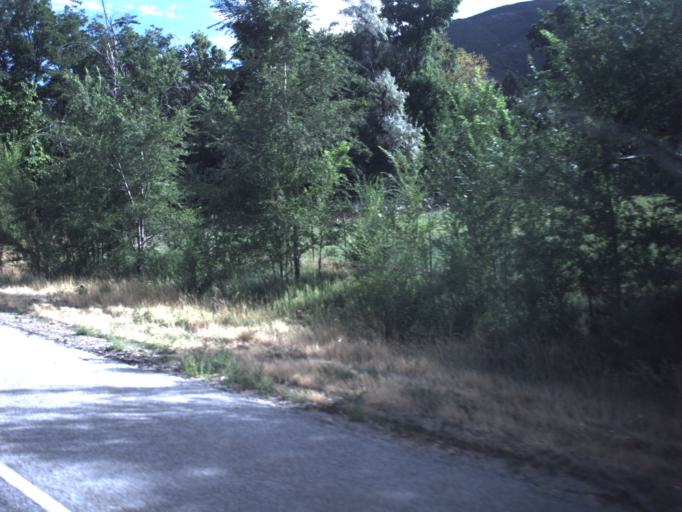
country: US
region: Utah
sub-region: Davis County
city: South Weber
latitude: 41.0869
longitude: -111.9107
